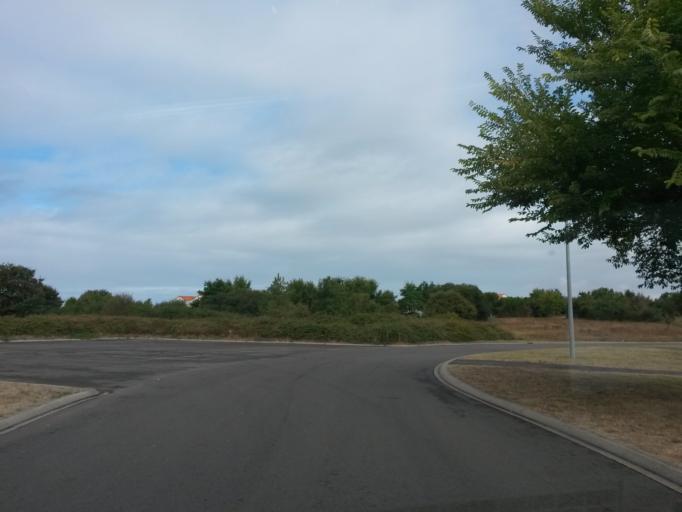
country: FR
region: Pays de la Loire
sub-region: Departement de la Vendee
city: Les Sables-d'Olonne
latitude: 46.5178
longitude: -1.7878
